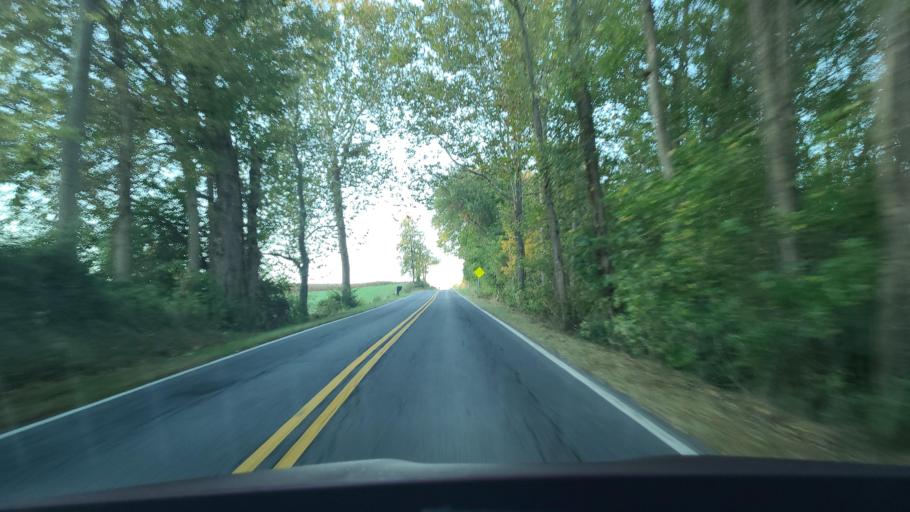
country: US
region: Maryland
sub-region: Frederick County
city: Jefferson
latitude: 39.3764
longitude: -77.5385
